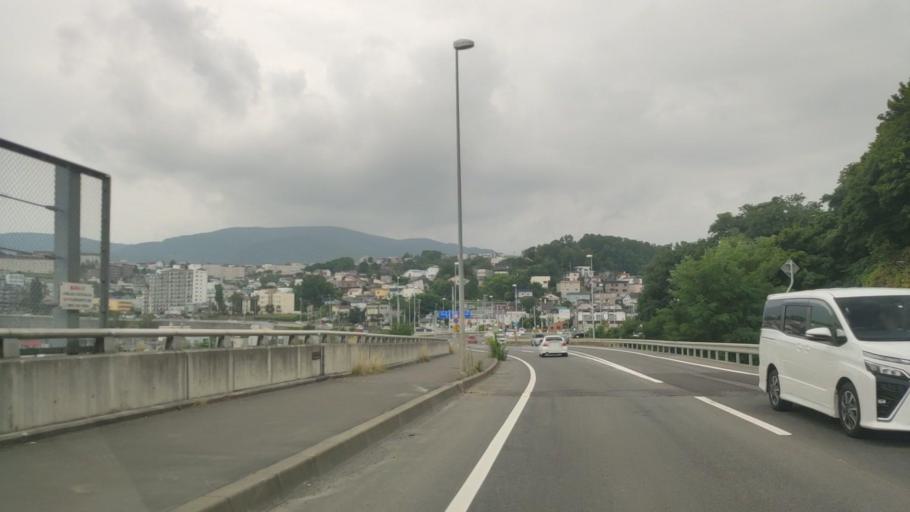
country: JP
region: Hokkaido
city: Otaru
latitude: 43.1801
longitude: 141.0373
